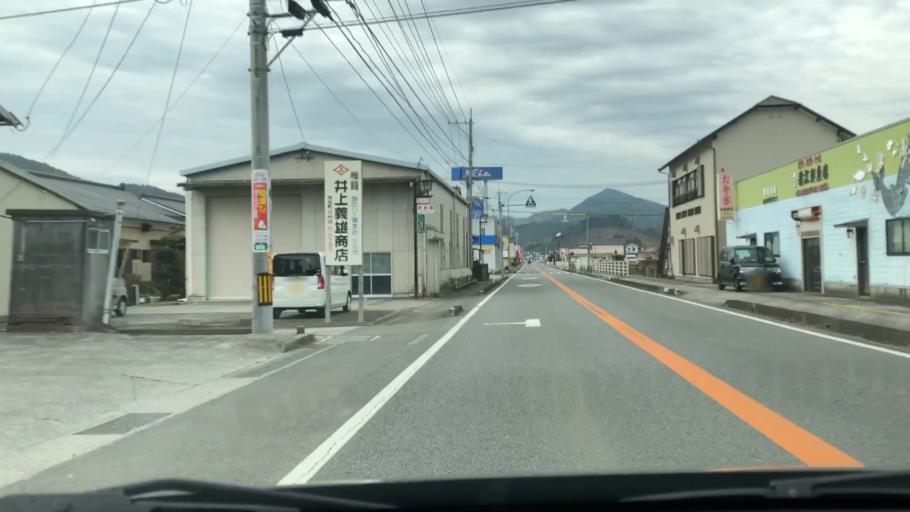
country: JP
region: Oita
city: Saiki
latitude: 32.9775
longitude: 131.8458
